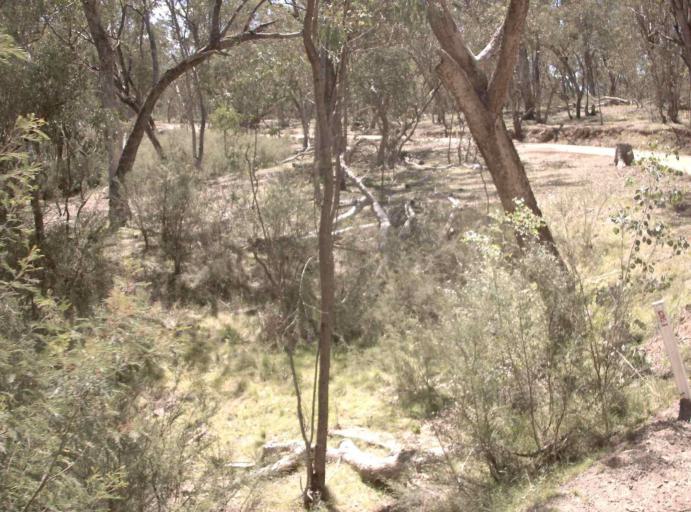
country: AU
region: New South Wales
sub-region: Snowy River
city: Jindabyne
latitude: -37.0526
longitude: 148.5388
